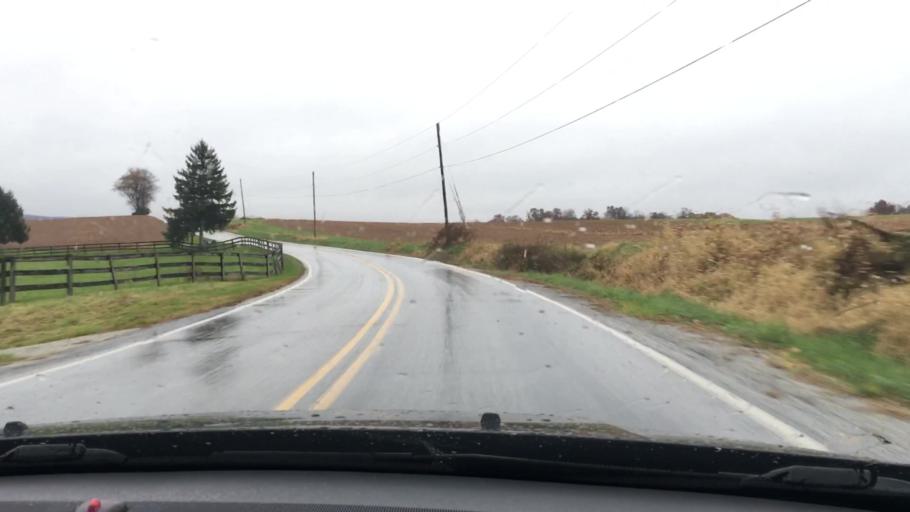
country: US
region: Pennsylvania
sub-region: York County
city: Susquehanna Trails
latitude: 39.8001
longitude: -76.4160
